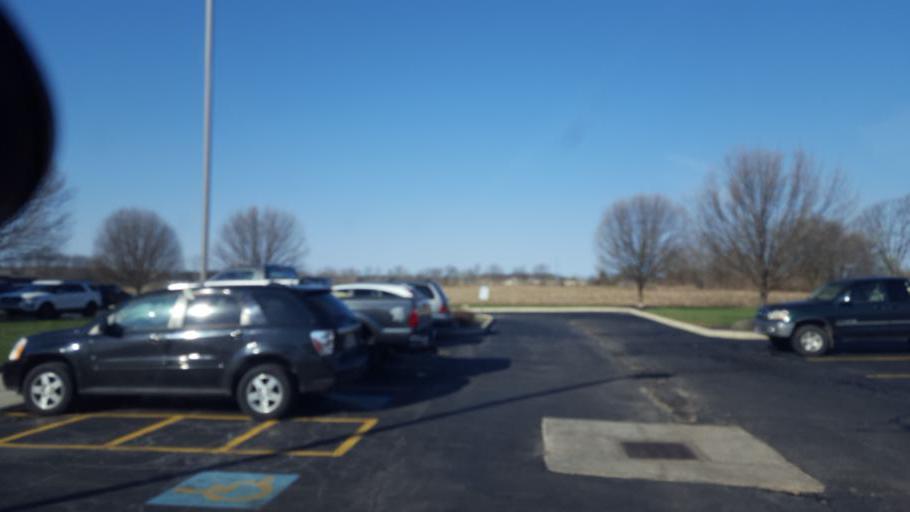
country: US
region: Ohio
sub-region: Marion County
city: Marion
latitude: 40.5630
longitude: -83.1078
